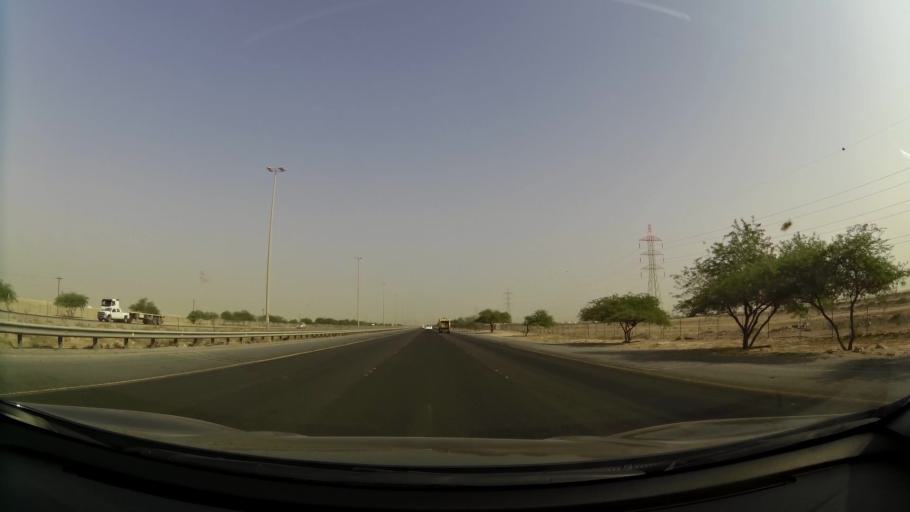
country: KW
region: Al Asimah
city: Ar Rabiyah
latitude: 29.2129
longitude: 47.8848
